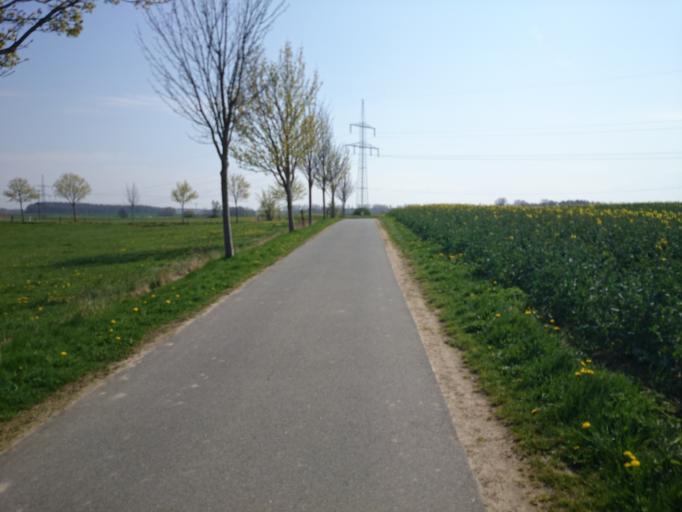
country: DE
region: Mecklenburg-Vorpommern
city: Broderstorf
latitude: 54.0732
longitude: 12.3611
